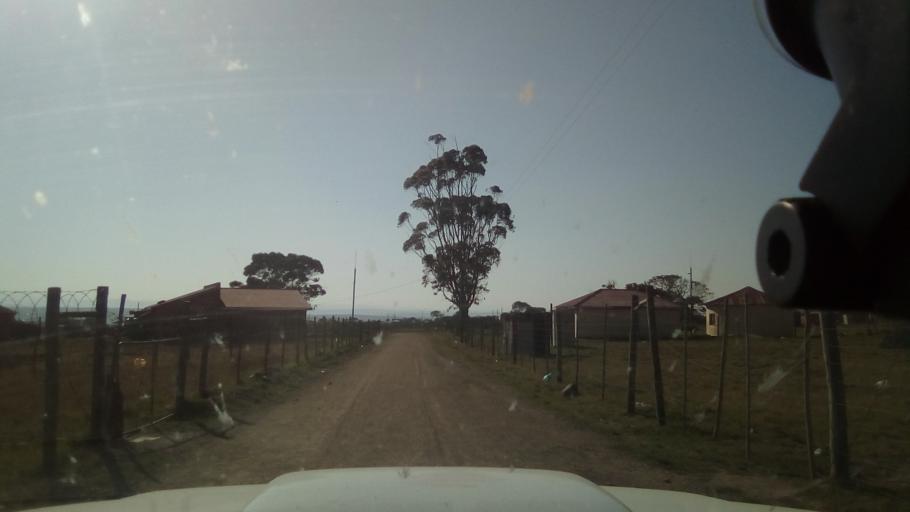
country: ZA
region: Eastern Cape
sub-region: Buffalo City Metropolitan Municipality
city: Bhisho
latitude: -32.9416
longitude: 27.3335
